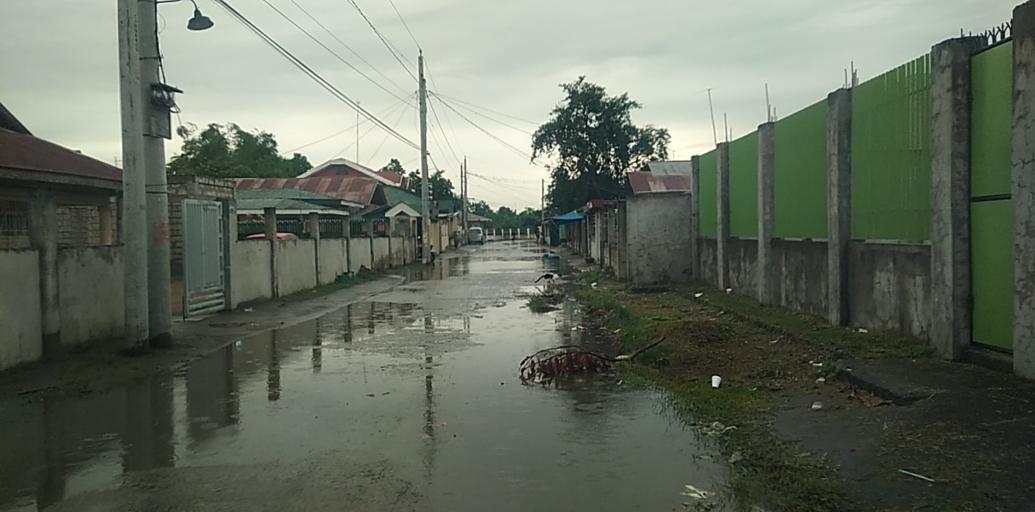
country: PH
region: Central Luzon
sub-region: Province of Pampanga
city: Arayat
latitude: 15.1412
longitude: 120.7326
